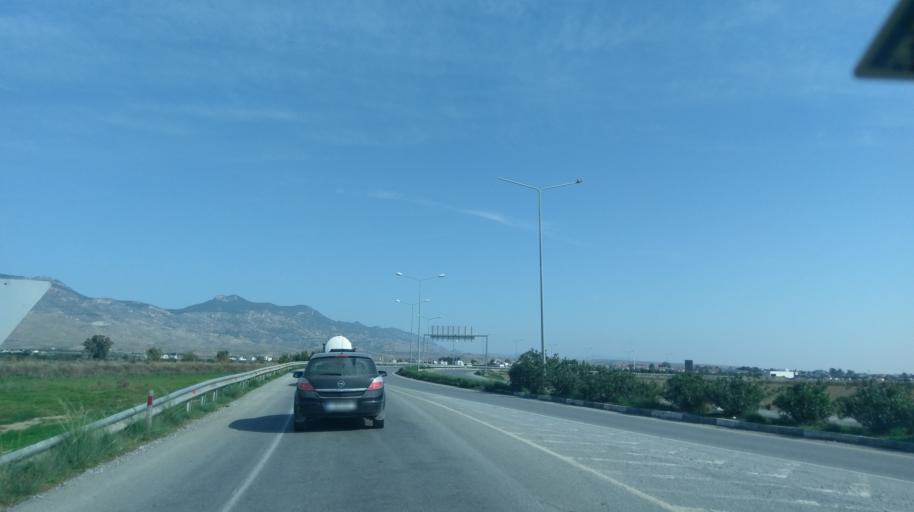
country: CY
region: Lefkosia
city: Geri
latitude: 35.2207
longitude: 33.4984
